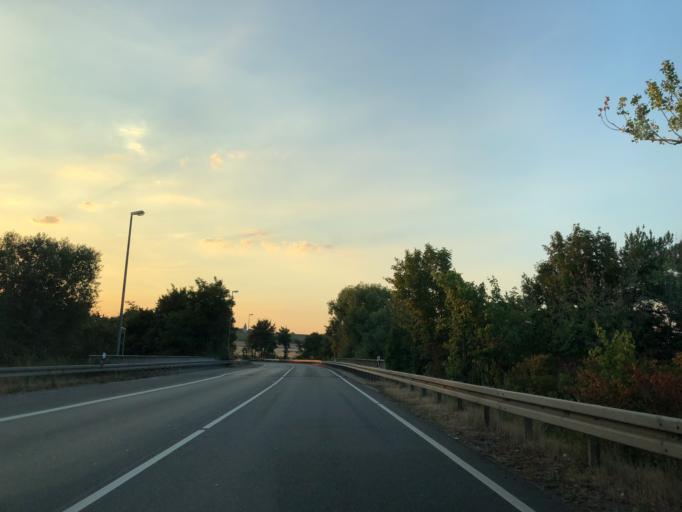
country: DE
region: Hesse
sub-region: Regierungsbezirk Darmstadt
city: Florsheim
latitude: 50.0091
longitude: 8.4163
